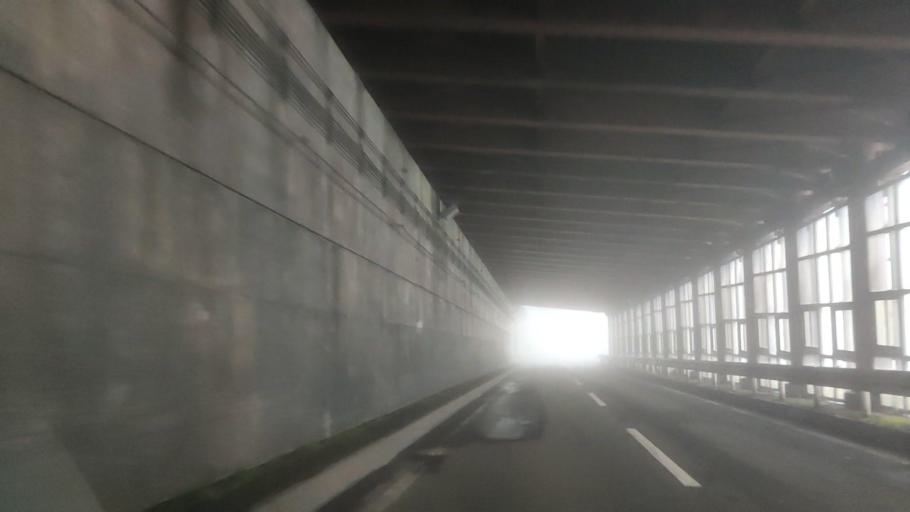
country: JP
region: Hokkaido
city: Date
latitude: 42.5510
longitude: 141.0829
